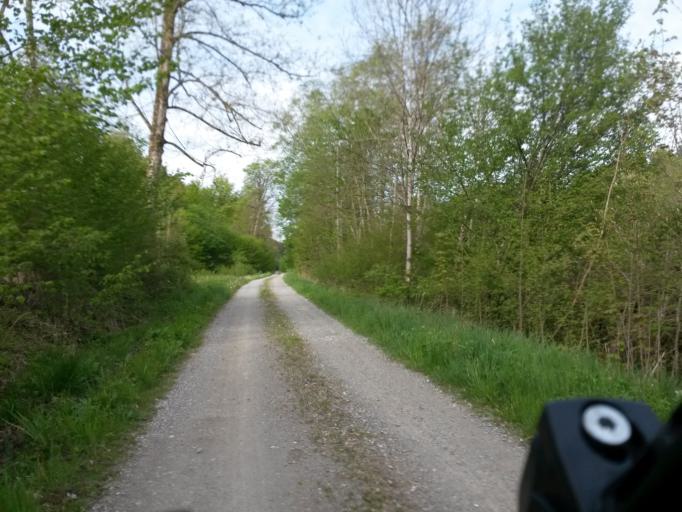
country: DE
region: Baden-Wuerttemberg
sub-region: Tuebingen Region
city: Baindt
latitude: 47.8927
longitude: 9.6723
